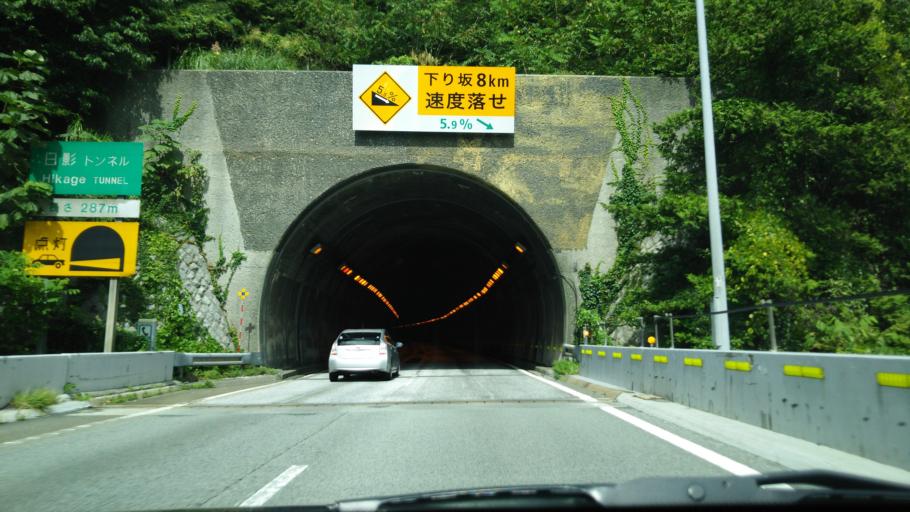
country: JP
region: Yamanashi
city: Enzan
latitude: 35.6446
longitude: 138.7640
